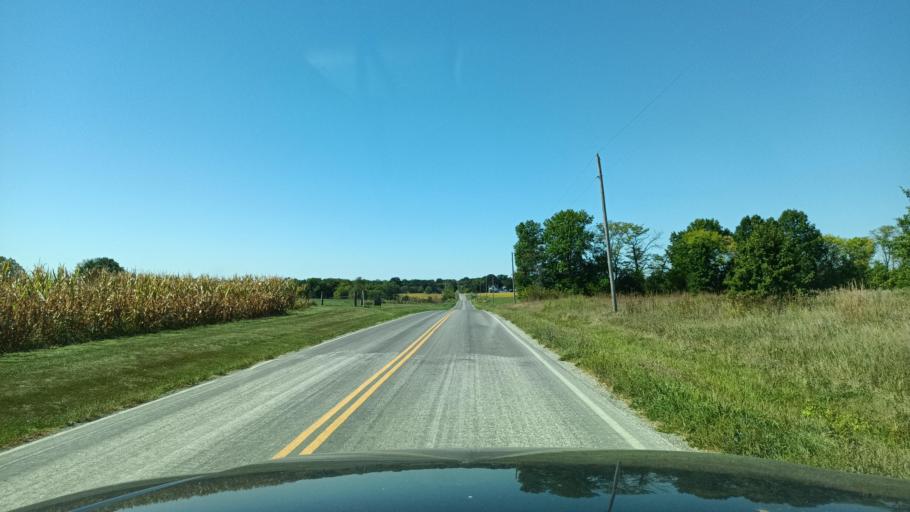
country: US
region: Missouri
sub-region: Macon County
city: La Plata
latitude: 40.0230
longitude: -92.5790
